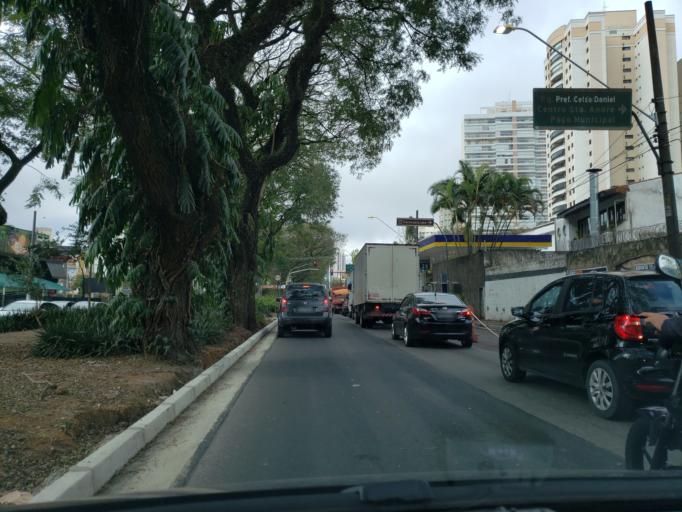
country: BR
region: Sao Paulo
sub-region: Santo Andre
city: Santo Andre
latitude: -23.6457
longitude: -46.5428
